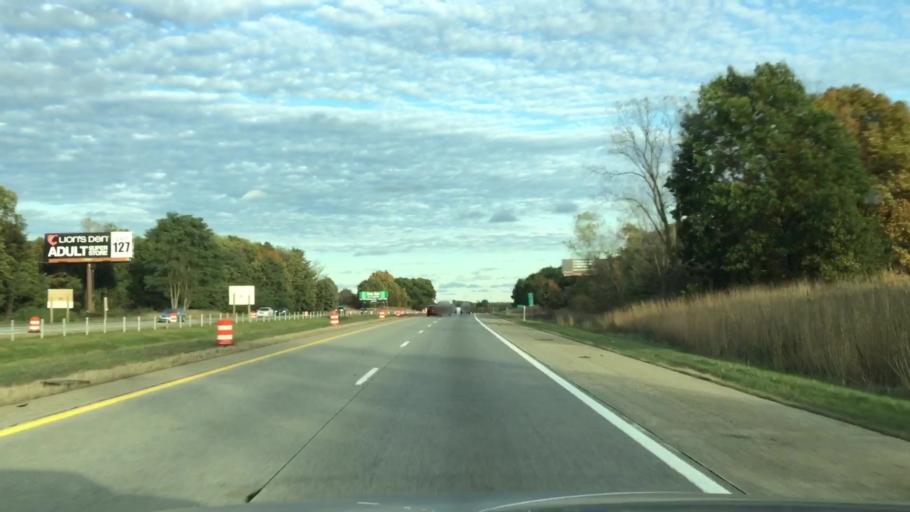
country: US
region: Michigan
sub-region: Calhoun County
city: Albion
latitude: 42.2645
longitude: -84.7303
